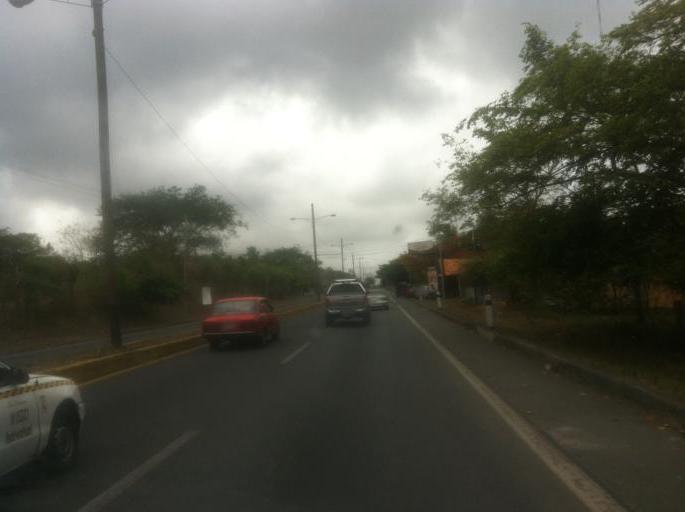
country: NI
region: Masaya
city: Nindiri
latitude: 12.0021
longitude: -86.1327
